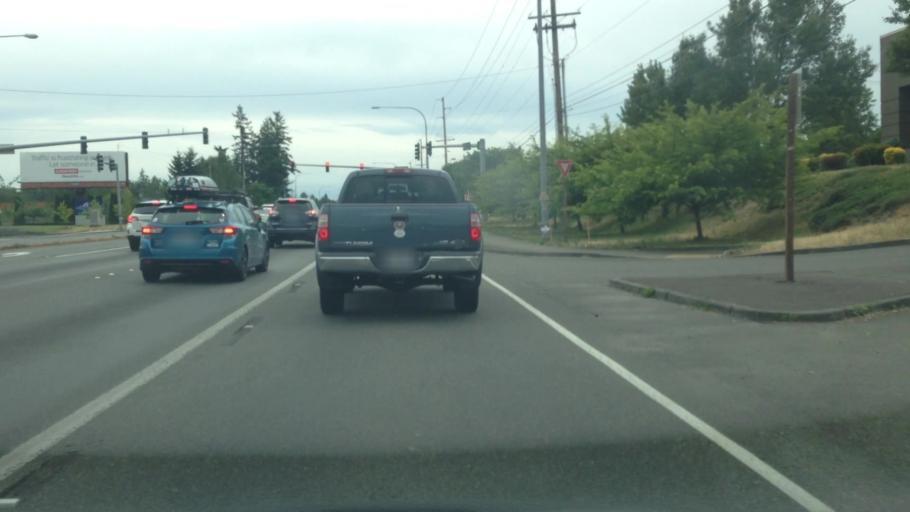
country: US
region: Washington
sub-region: Pierce County
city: South Hill
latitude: 47.1119
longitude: -122.2935
